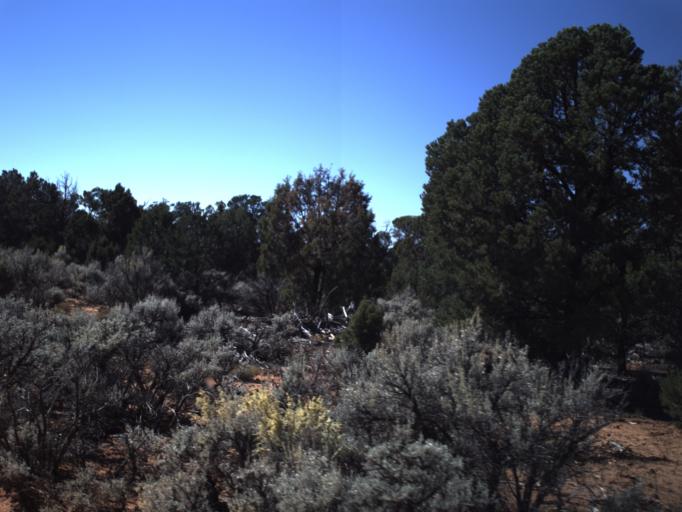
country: US
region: Utah
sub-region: San Juan County
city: Blanding
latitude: 37.5805
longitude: -109.8859
